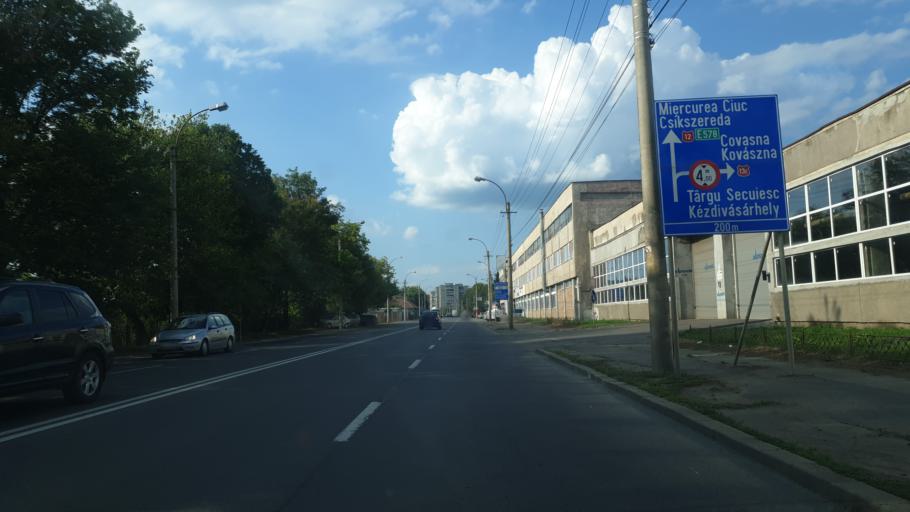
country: RO
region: Covasna
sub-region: Municipiul Sfantu Gheorghe
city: Sfantu-Gheorghe
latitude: 45.8542
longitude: 25.8066
